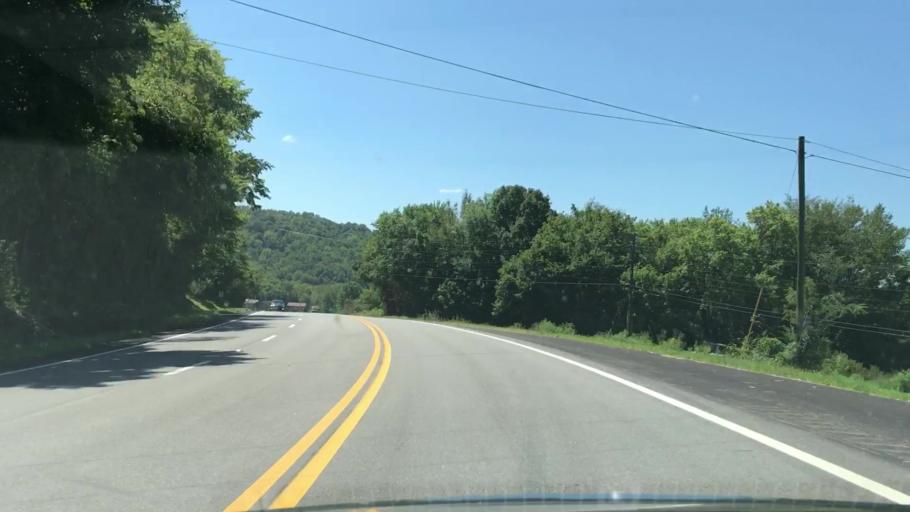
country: US
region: Tennessee
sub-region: Clay County
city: Celina
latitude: 36.5472
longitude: -85.5006
